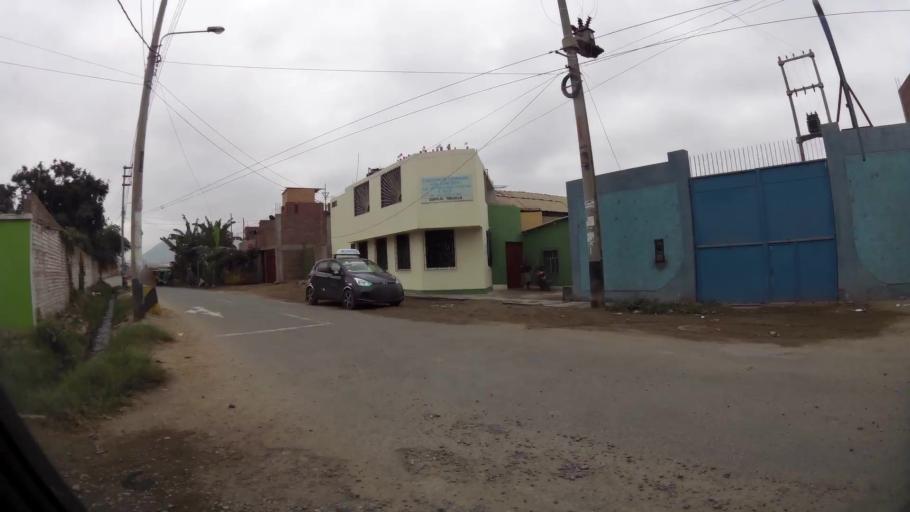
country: PE
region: La Libertad
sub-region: Provincia de Trujillo
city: La Esperanza
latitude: -8.0960
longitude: -79.0555
